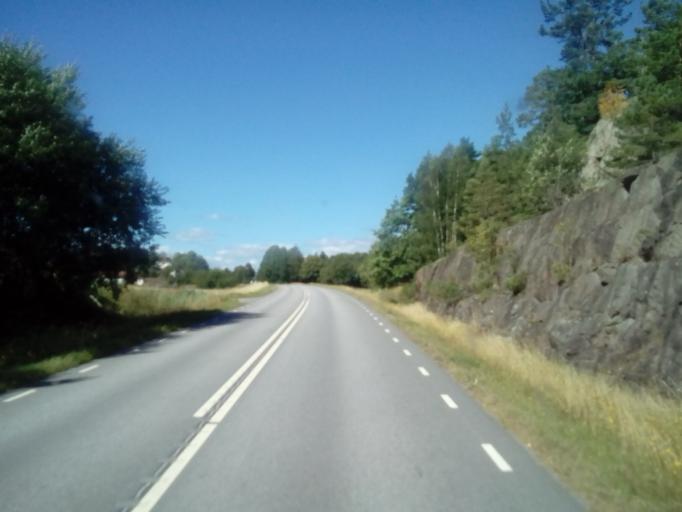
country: SE
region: Kalmar
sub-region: Vimmerby Kommun
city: Sodra Vi
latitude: 57.9220
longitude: 15.9395
